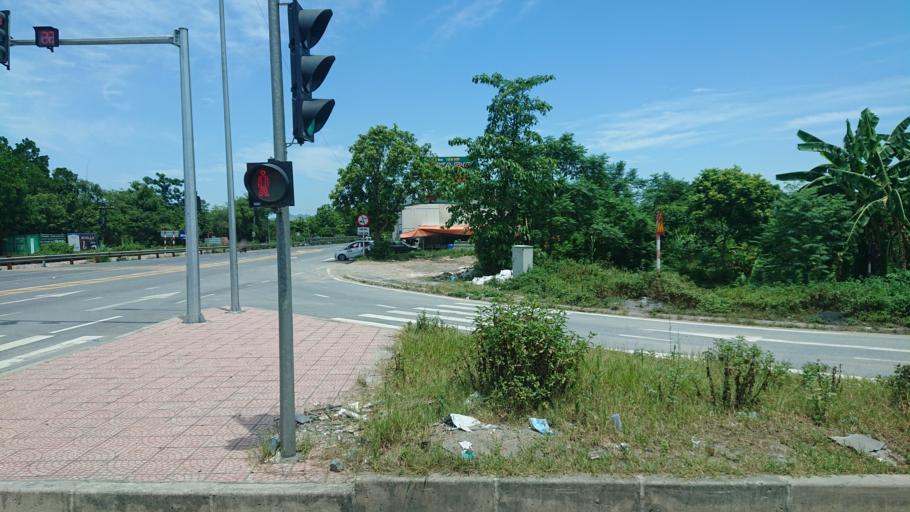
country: VN
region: Ha Nam
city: Thanh Pho Phu Ly
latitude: 20.5199
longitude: 105.9442
